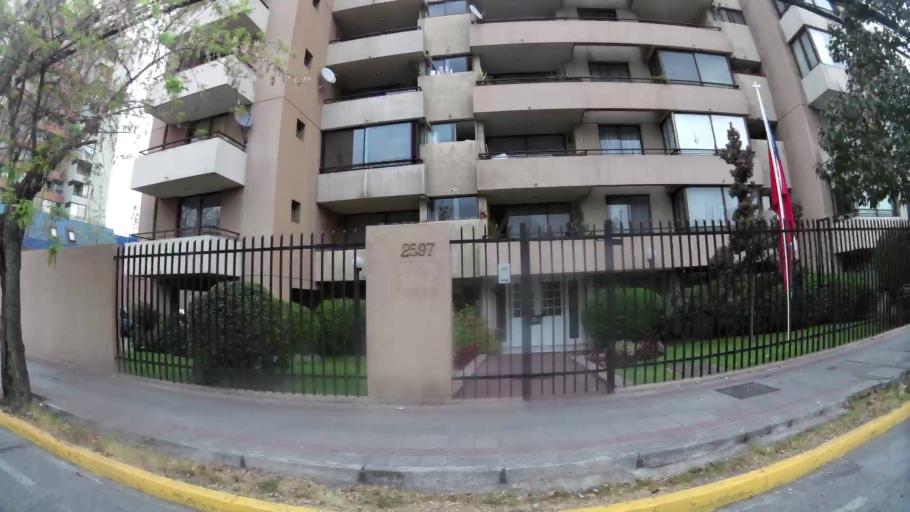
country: CL
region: Santiago Metropolitan
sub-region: Provincia de Santiago
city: Villa Presidente Frei, Nunoa, Santiago, Chile
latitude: -33.4513
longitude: -70.6098
